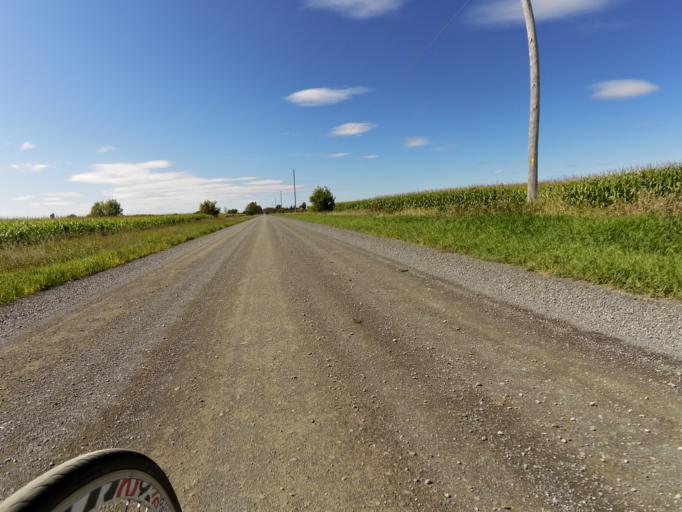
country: CA
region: Ontario
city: Bells Corners
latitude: 45.2231
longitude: -75.8437
